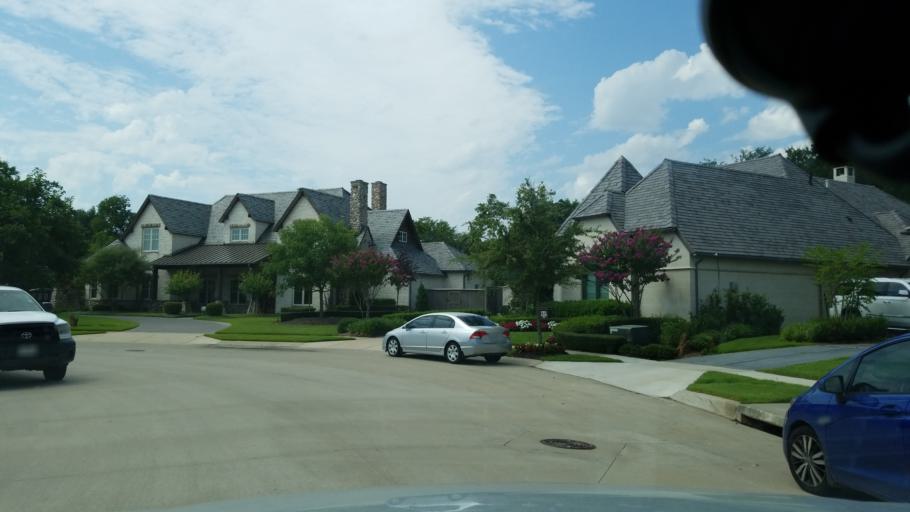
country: US
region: Texas
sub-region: Dallas County
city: Coppell
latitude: 32.9610
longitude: -96.9951
